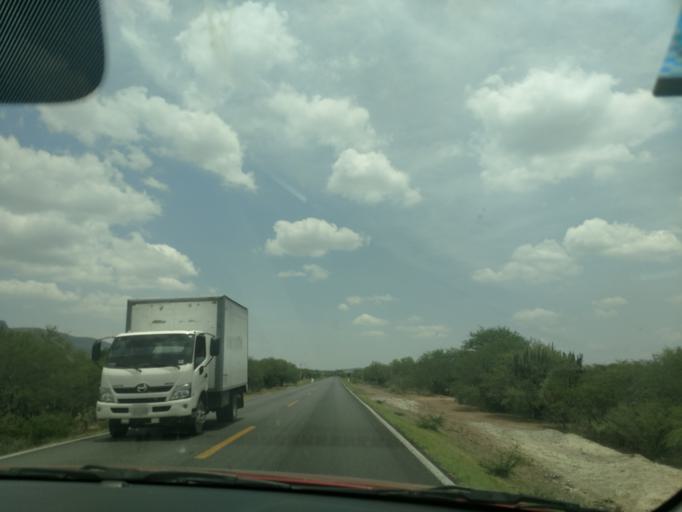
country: MX
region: San Luis Potosi
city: Villa Juarez
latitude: 22.0185
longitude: -100.3920
